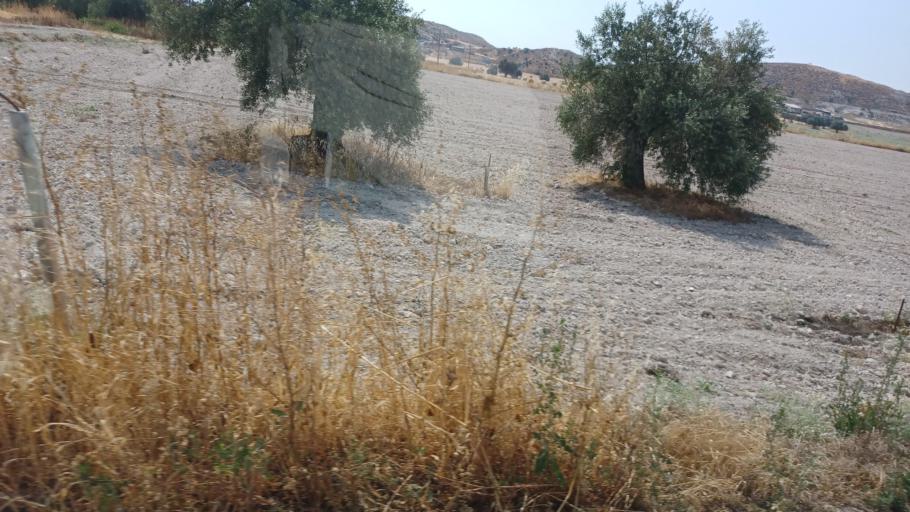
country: CY
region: Larnaka
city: Aradippou
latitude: 34.9230
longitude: 33.5377
